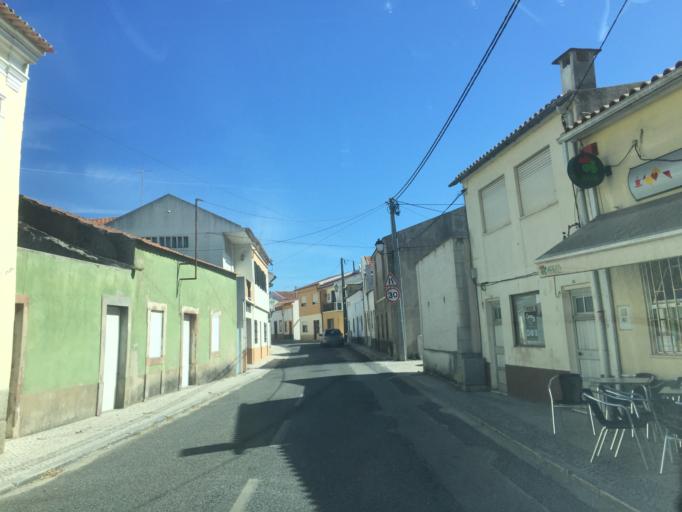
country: PT
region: Coimbra
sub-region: Figueira da Foz
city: Tavarede
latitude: 40.2144
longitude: -8.8553
